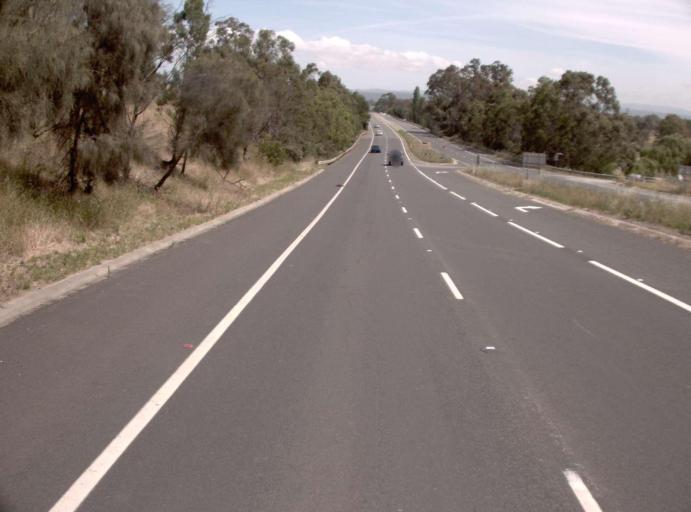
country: AU
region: Victoria
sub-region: Wellington
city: Heyfield
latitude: -38.1400
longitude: 146.7935
